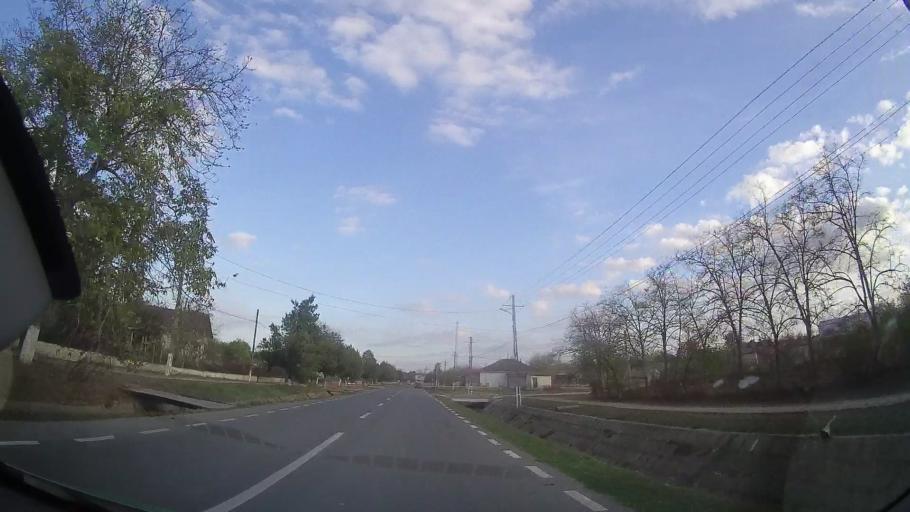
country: RO
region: Constanta
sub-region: Comuna Independenta
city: Independenta
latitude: 43.9531
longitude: 28.0790
